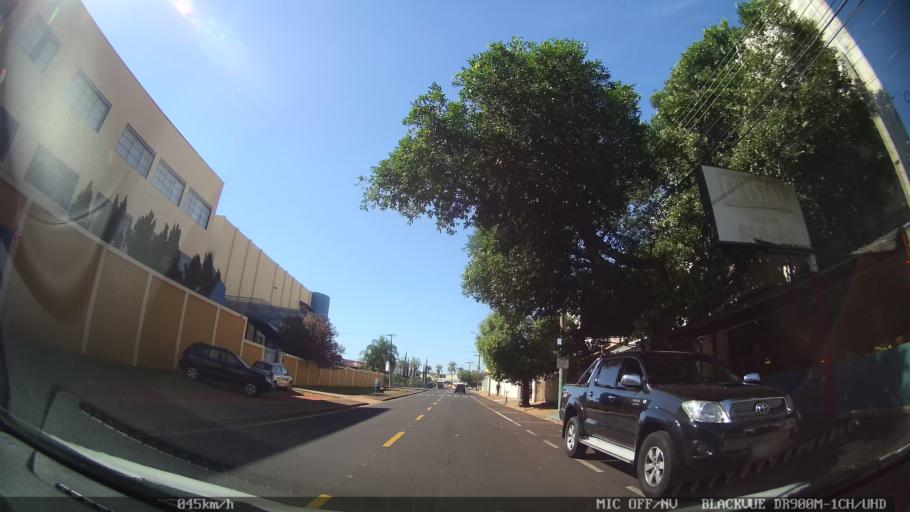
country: BR
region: Sao Paulo
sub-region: Sao Jose Do Rio Preto
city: Sao Jose do Rio Preto
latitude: -20.8097
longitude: -49.4016
